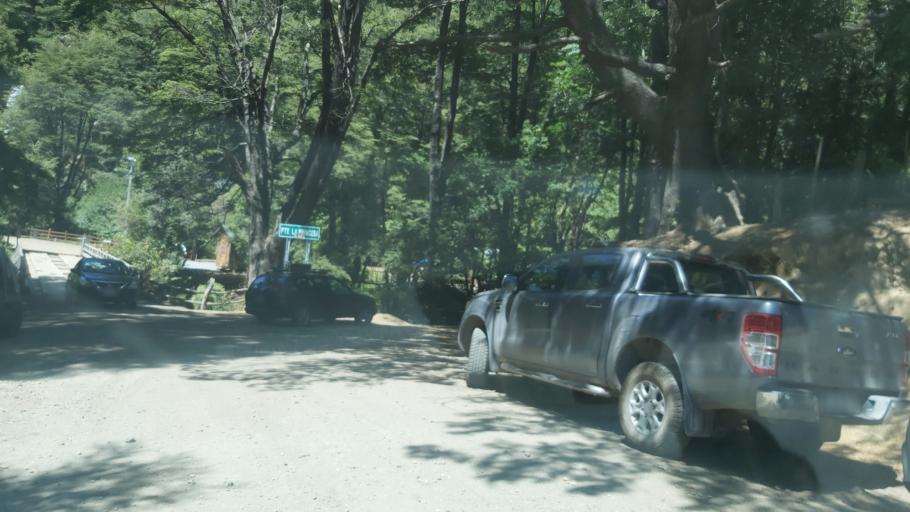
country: CL
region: Araucania
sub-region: Provincia de Cautin
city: Vilcun
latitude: -38.4739
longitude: -71.6737
